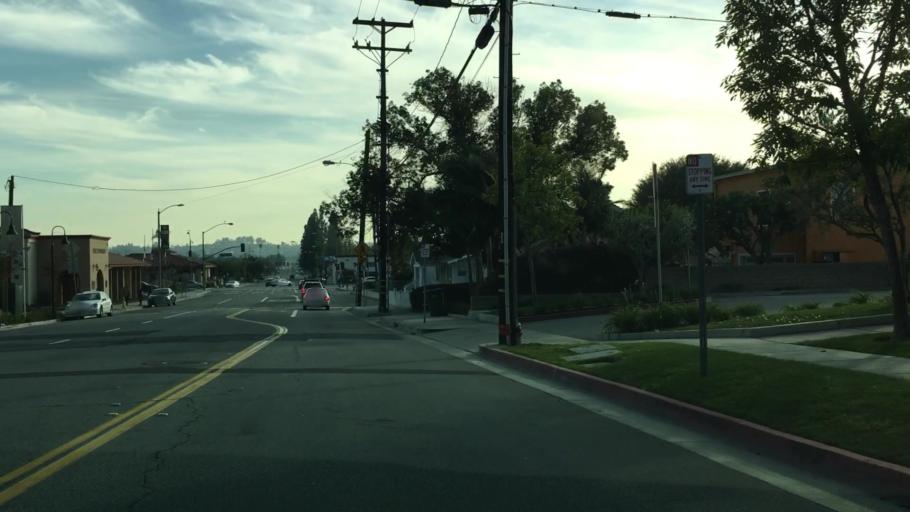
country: US
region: California
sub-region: Orange County
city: La Habra
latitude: 33.9333
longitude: -117.9462
